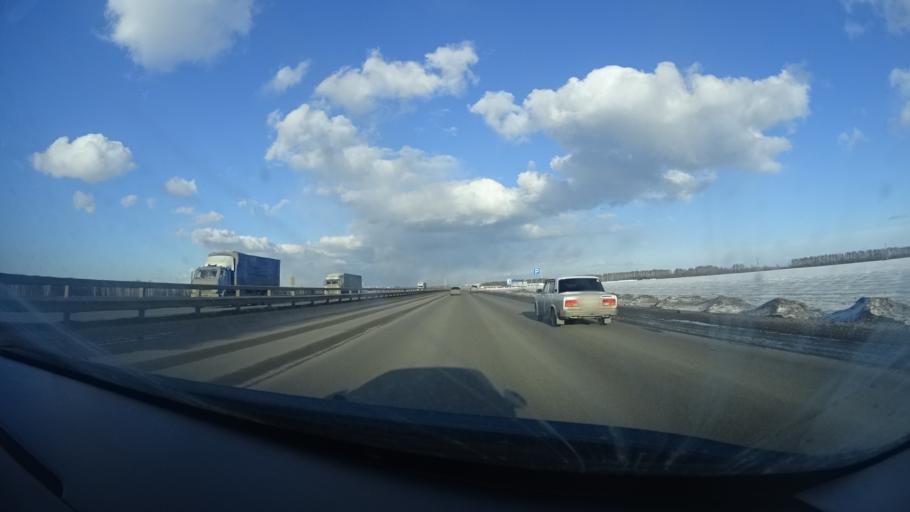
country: RU
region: Bashkortostan
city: Avdon
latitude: 54.6712
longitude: 55.7705
